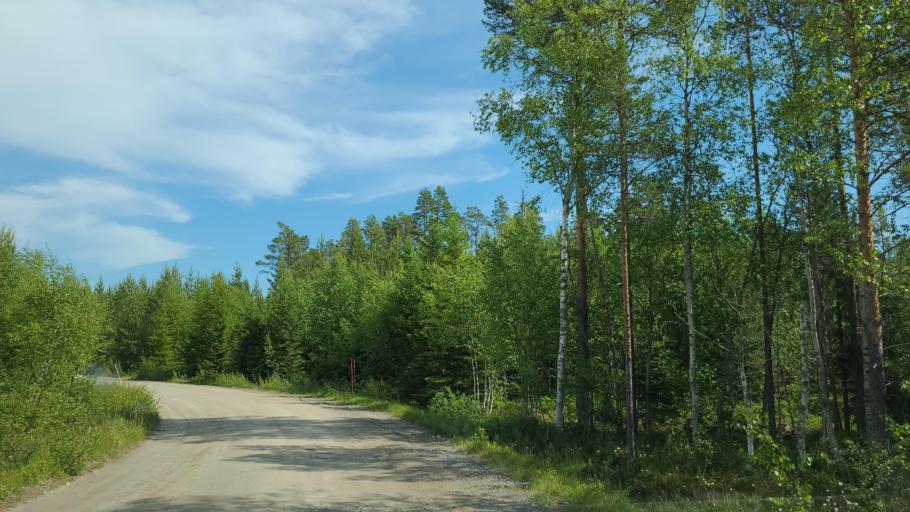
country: SE
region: Vaesterbotten
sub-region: Robertsfors Kommun
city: Robertsfors
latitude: 64.2272
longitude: 21.0432
